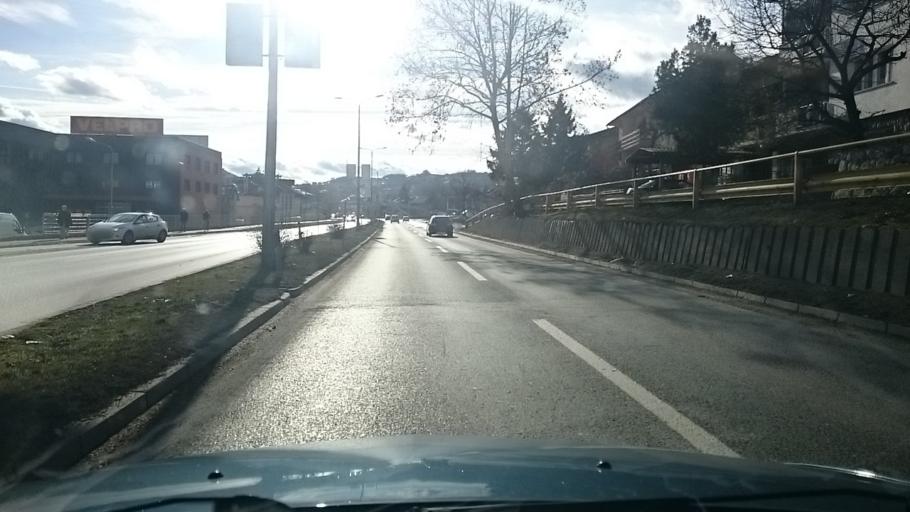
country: BA
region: Republika Srpska
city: Banja Luka
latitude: 44.7776
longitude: 17.1843
